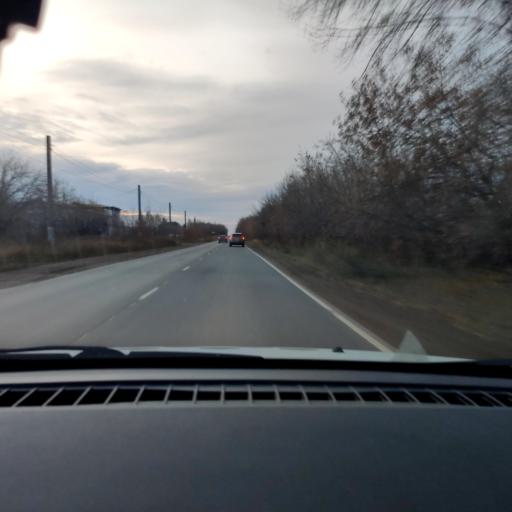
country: RU
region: Perm
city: Gamovo
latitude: 57.9073
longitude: 56.1664
